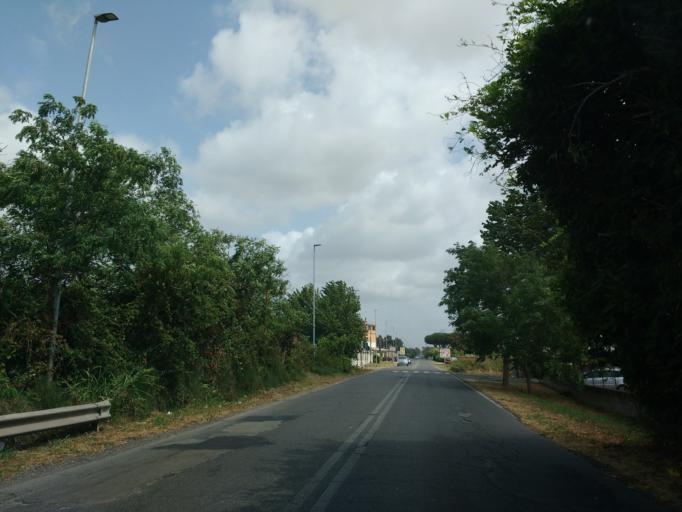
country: IT
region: Latium
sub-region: Citta metropolitana di Roma Capitale
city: Marina di Ardea-Tor San Lorenzo
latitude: 41.5571
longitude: 12.5366
